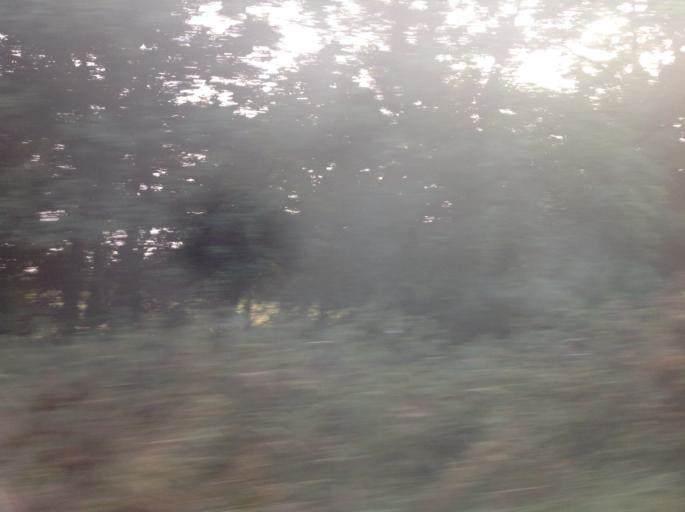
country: GB
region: England
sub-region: Suffolk
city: Felixstowe
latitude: 51.9821
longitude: 1.3254
